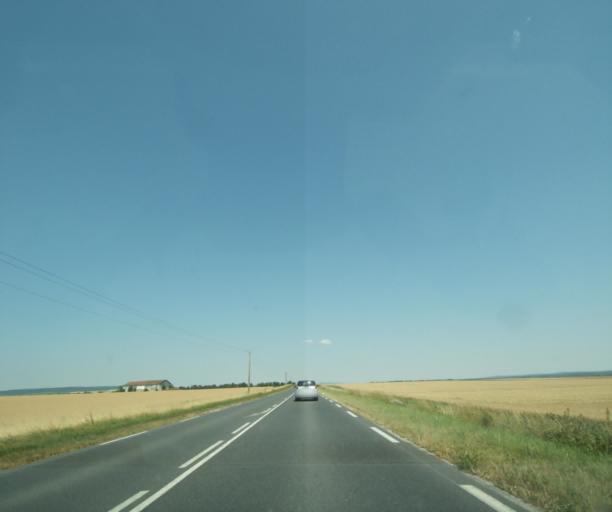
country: FR
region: Champagne-Ardenne
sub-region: Departement de la Marne
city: Mourmelon-le-Grand
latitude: 49.0808
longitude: 4.2824
